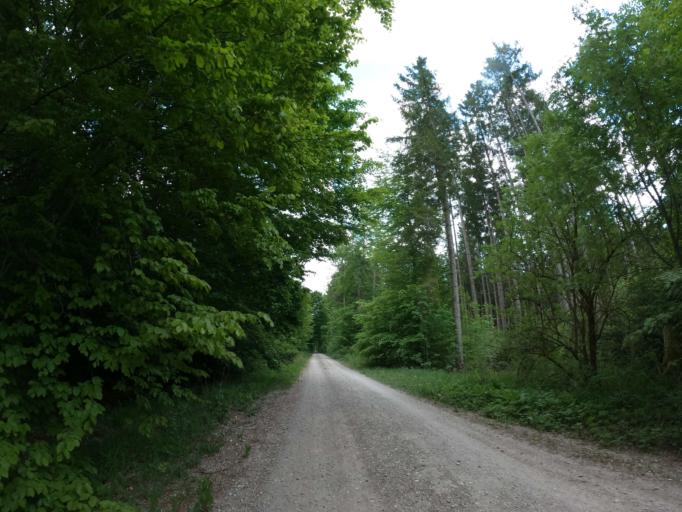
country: DE
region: Bavaria
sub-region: Upper Bavaria
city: Aying
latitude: 47.9670
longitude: 11.7263
